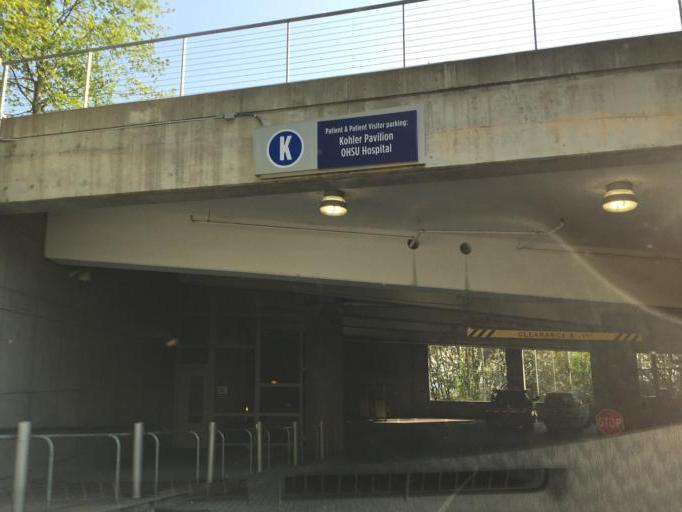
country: US
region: Oregon
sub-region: Multnomah County
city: Portland
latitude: 45.5002
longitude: -122.6839
